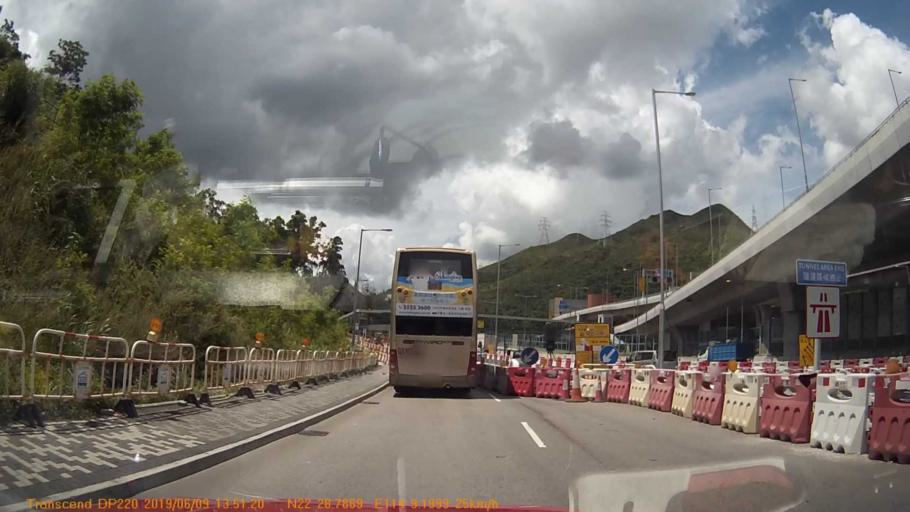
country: HK
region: Tai Po
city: Tai Po
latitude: 22.4800
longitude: 114.1534
